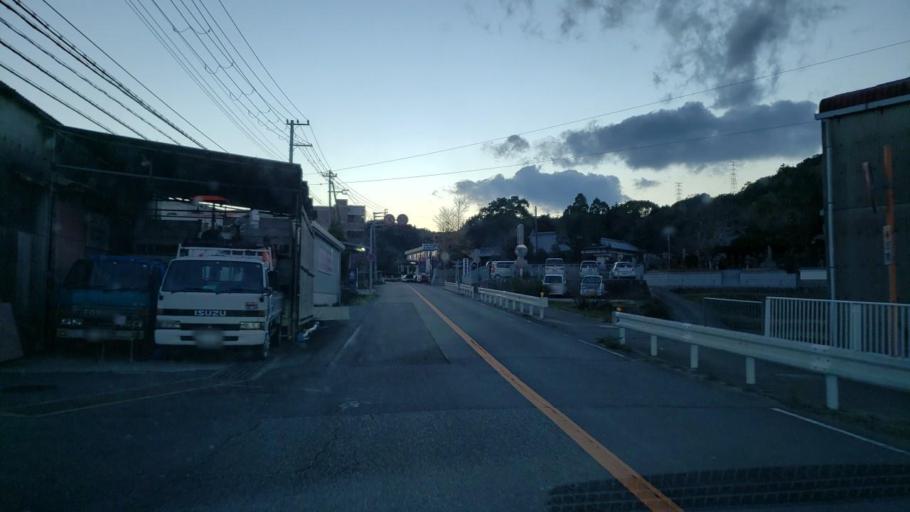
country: JP
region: Hyogo
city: Fukura
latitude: 34.3028
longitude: 134.7376
